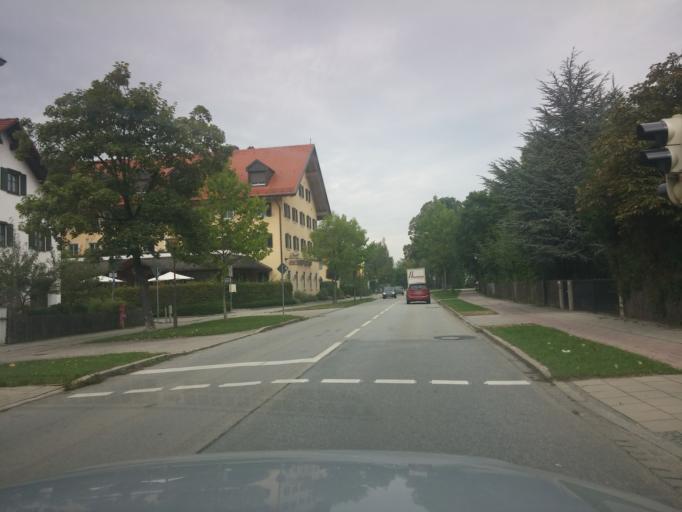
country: DE
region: Bavaria
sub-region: Upper Bavaria
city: Aschheim
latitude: 48.1734
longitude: 11.7155
